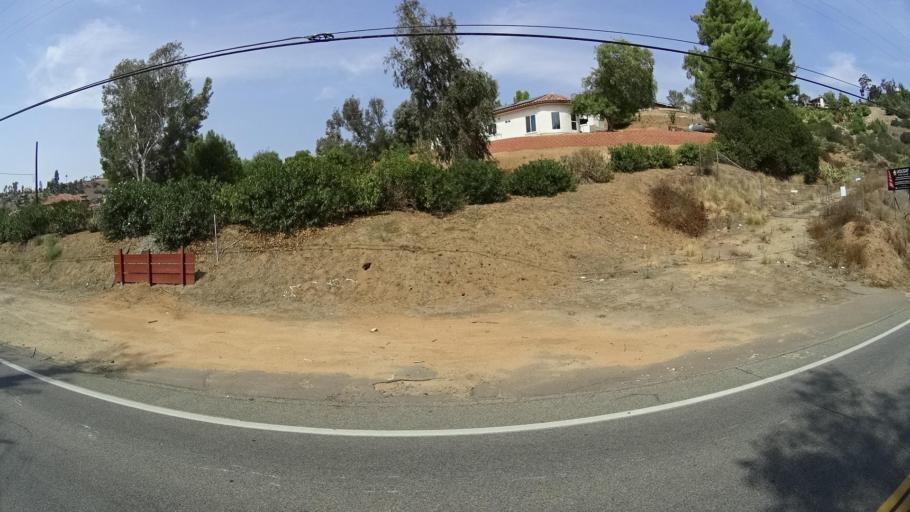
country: US
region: California
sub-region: San Diego County
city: Escondido
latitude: 33.0858
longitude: -117.0263
